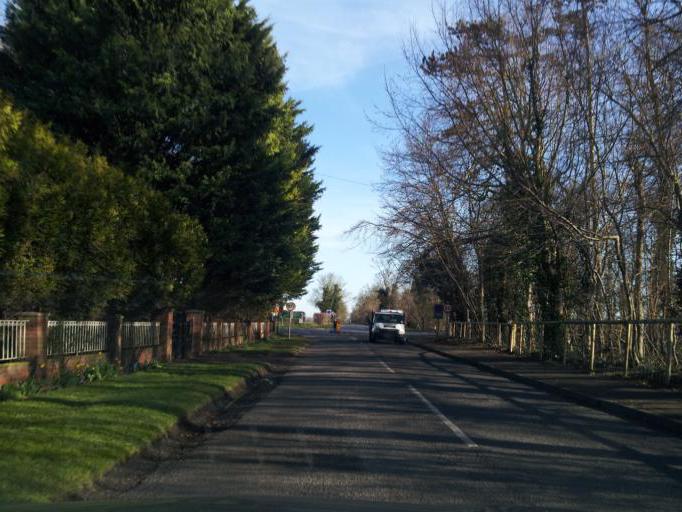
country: GB
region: England
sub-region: Cambridgeshire
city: Meldreth
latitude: 52.1086
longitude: 0.0419
